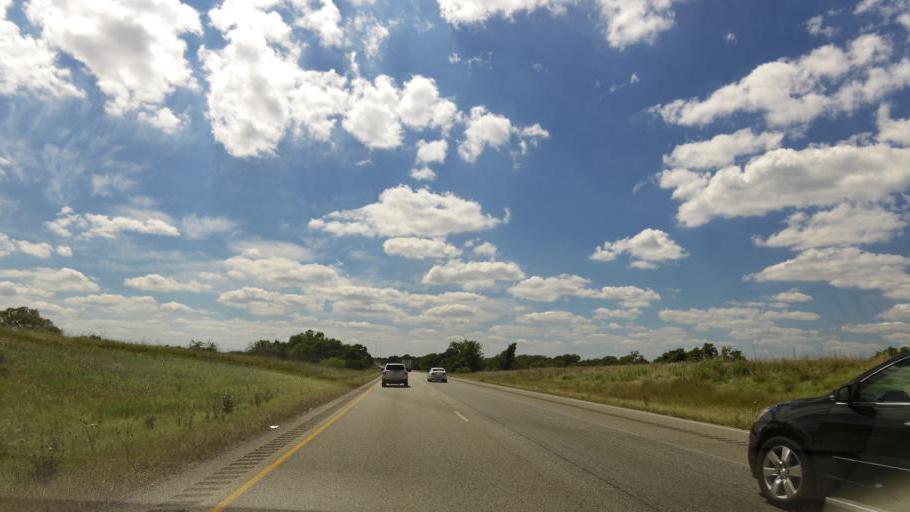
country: US
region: Texas
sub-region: Fayette County
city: Flatonia
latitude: 29.6977
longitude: -97.0429
